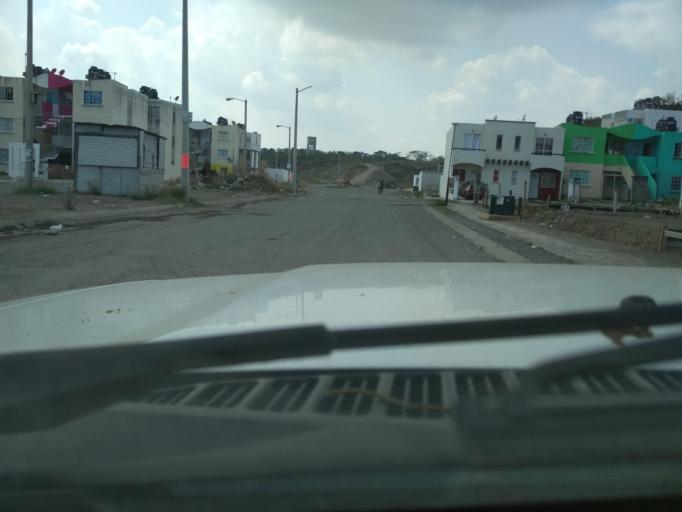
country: MX
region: Veracruz
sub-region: Veracruz
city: Lomas de Rio Medio Cuatro
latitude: 19.1859
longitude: -96.2126
